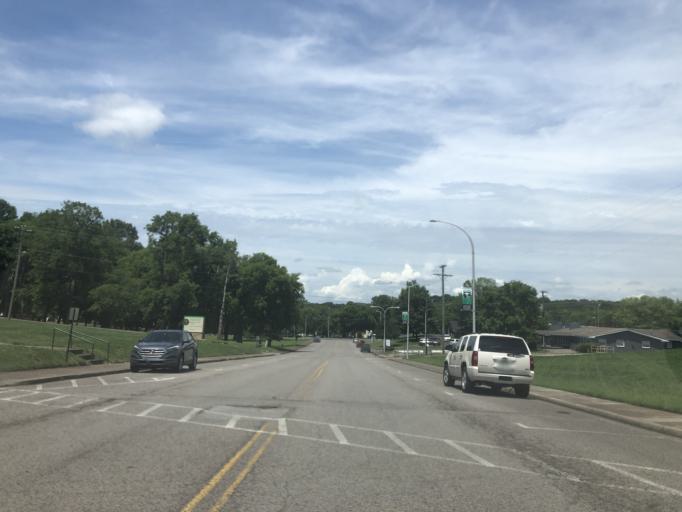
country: US
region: Tennessee
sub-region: Davidson County
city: Lakewood
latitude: 36.2540
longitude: -86.6833
